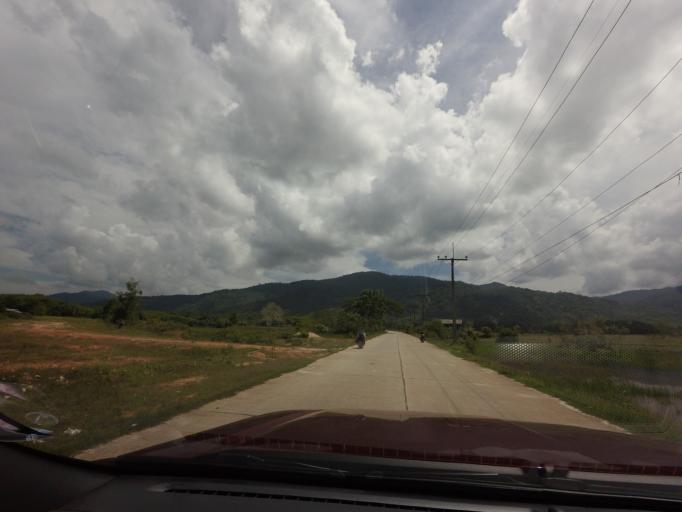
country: TH
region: Narathiwat
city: Bacho
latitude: 6.4876
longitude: 101.6637
